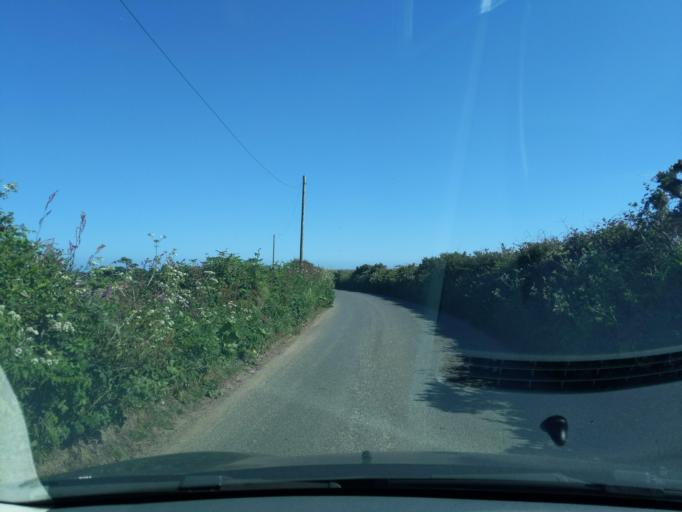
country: GB
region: England
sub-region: Cornwall
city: St. Buryan
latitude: 50.0731
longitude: -5.6144
